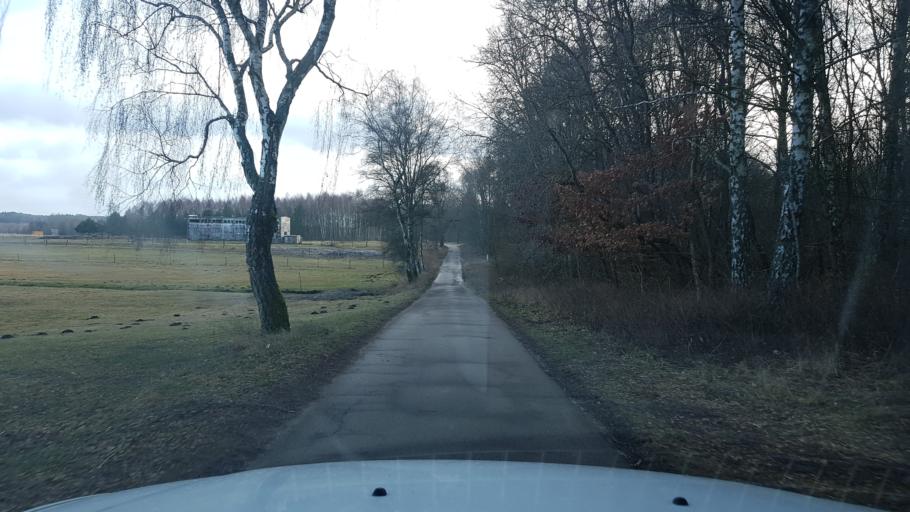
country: PL
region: West Pomeranian Voivodeship
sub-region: Powiat szczecinecki
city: Borne Sulinowo
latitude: 53.6287
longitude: 16.6126
